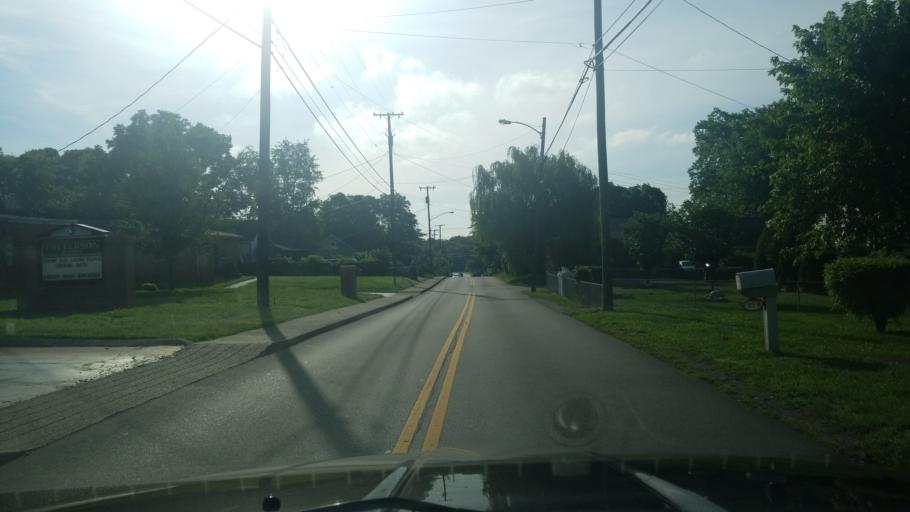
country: US
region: Tennessee
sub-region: Davidson County
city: Oak Hill
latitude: 36.1153
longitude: -86.7457
